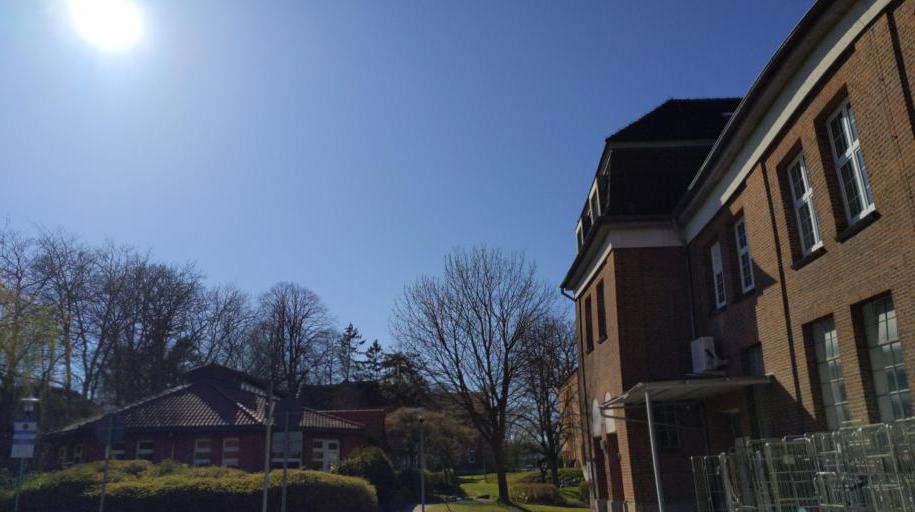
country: DE
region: Schleswig-Holstein
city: Neustadt in Holstein
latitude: 54.1065
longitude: 10.7971
